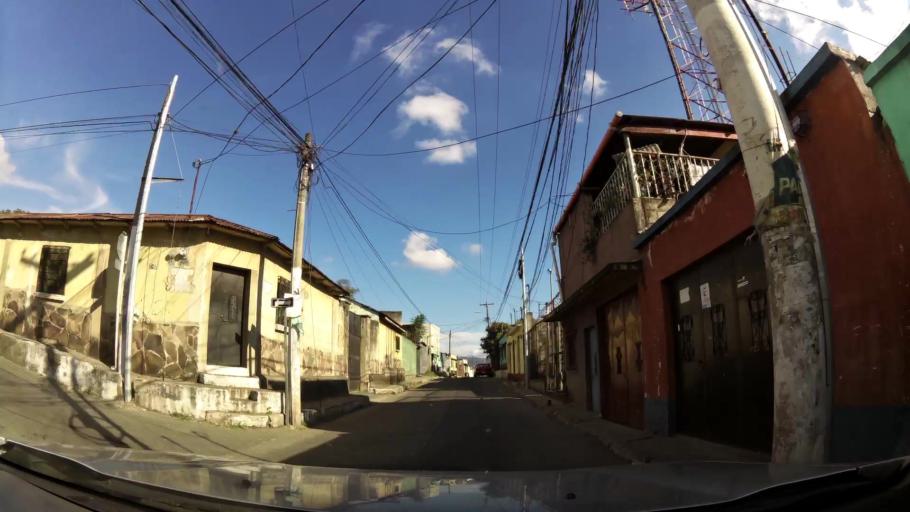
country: GT
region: Guatemala
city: Villa Nueva
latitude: 14.5243
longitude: -90.5820
